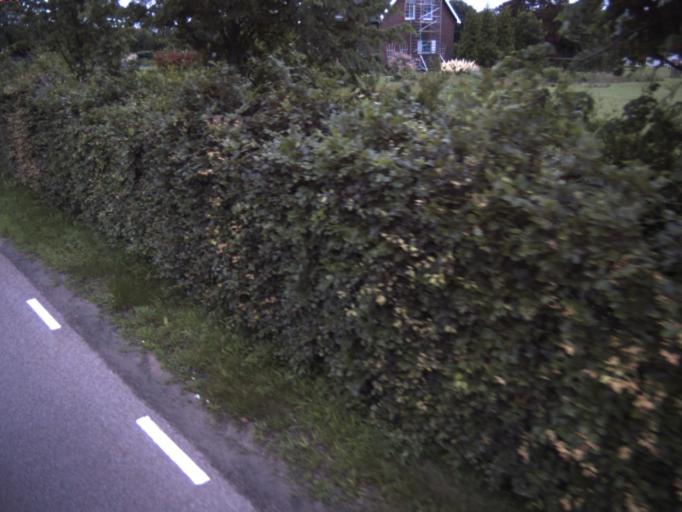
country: SE
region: Skane
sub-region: Helsingborg
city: Odakra
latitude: 56.1037
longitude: 12.7351
